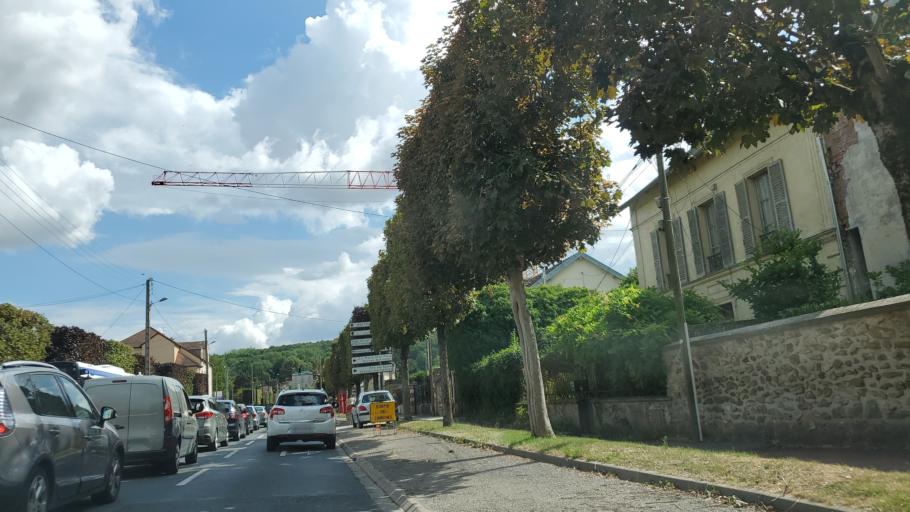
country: FR
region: Ile-de-France
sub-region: Departement de Seine-et-Marne
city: Coulommiers
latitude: 48.8044
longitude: 3.0850
